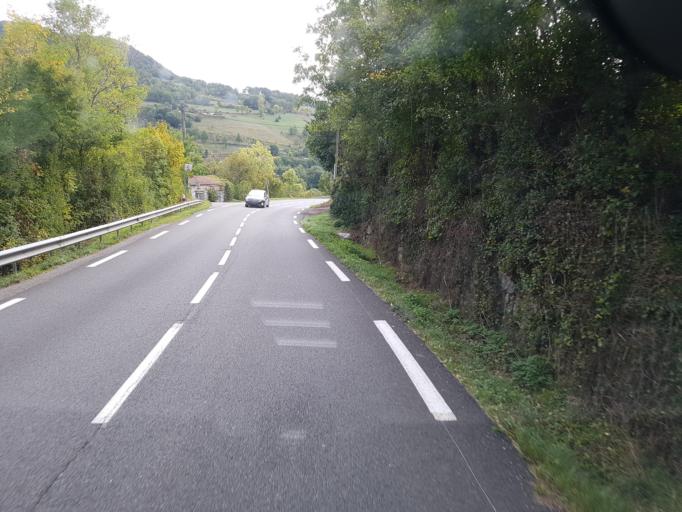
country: FR
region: Midi-Pyrenees
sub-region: Departement de l'Aveyron
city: Saint-Affrique
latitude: 43.9678
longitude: 2.8987
